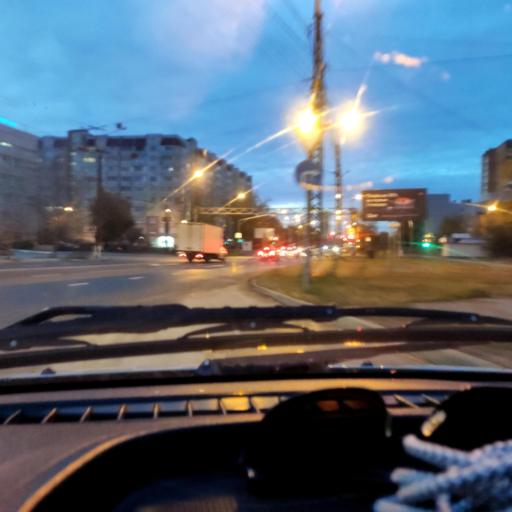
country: RU
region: Samara
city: Zhigulevsk
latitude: 53.4825
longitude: 49.4861
